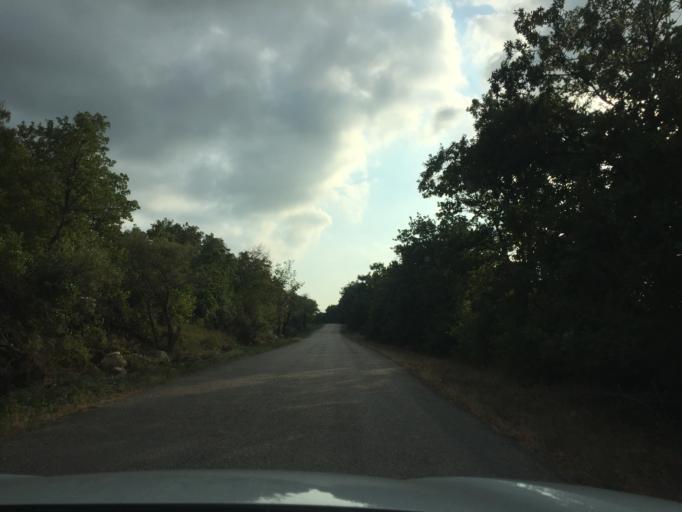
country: TR
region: Balikesir
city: Gonen
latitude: 40.0407
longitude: 27.5765
